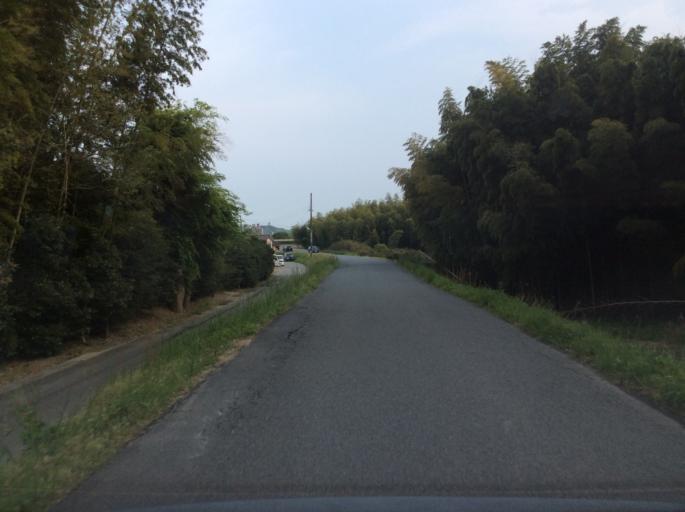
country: JP
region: Fukushima
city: Iwaki
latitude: 37.0670
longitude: 140.8959
